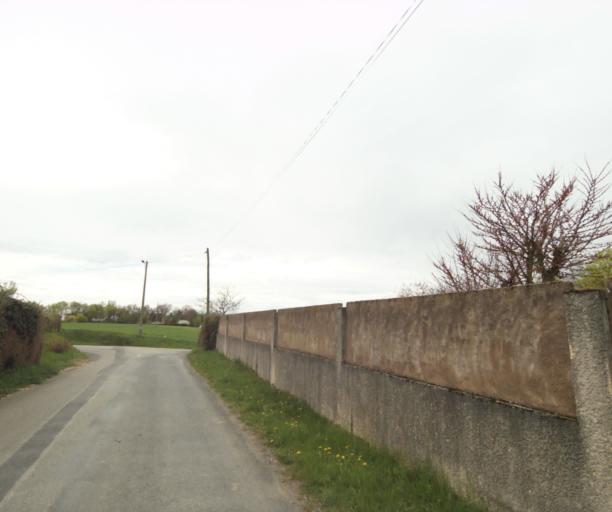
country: FR
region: Bourgogne
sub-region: Departement de Saone-et-Loire
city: Charnay-les-Macon
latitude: 46.3033
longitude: 4.7793
